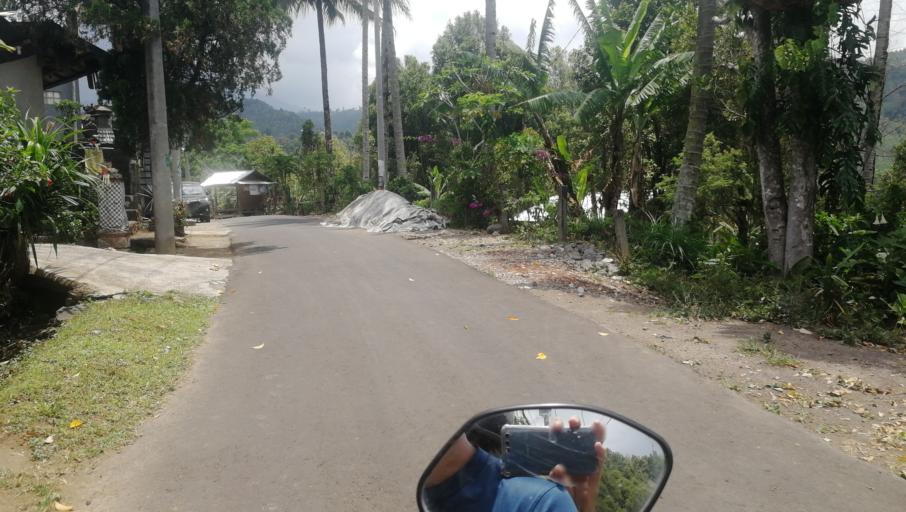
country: ID
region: Bali
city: Munduk
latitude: -8.2892
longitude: 115.0419
